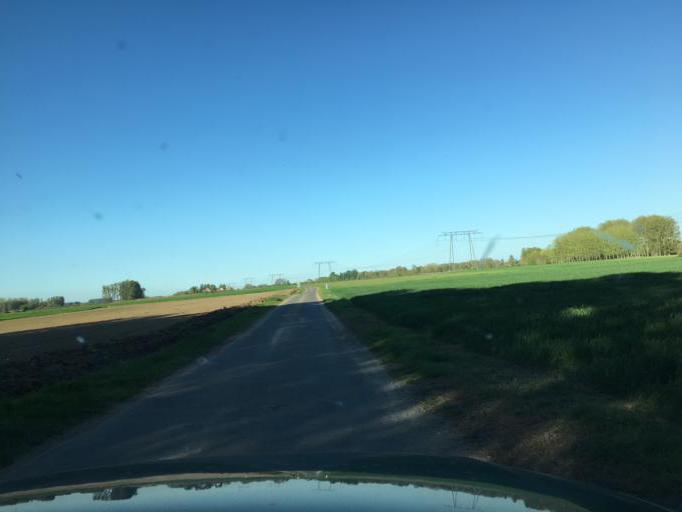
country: FR
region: Centre
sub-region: Departement du Loiret
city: Tavers
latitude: 47.7450
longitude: 1.6424
